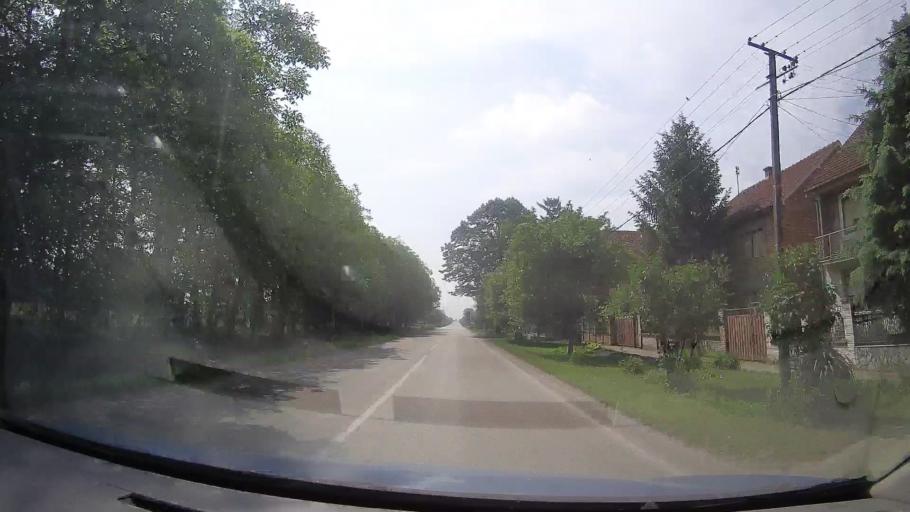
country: RS
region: Autonomna Pokrajina Vojvodina
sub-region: Juznobanatski Okrug
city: Kovacica
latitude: 45.1009
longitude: 20.6249
